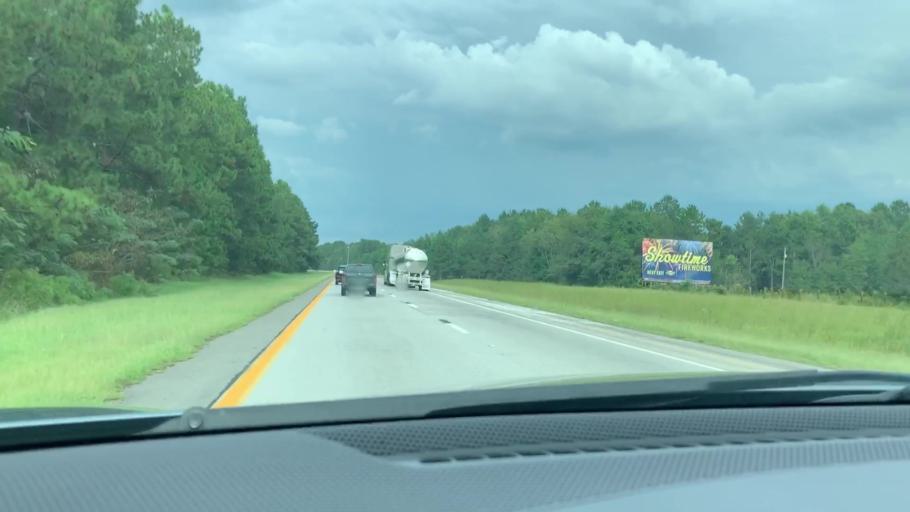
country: US
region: South Carolina
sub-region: Dorchester County
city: Saint George
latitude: 33.1389
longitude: -80.6305
